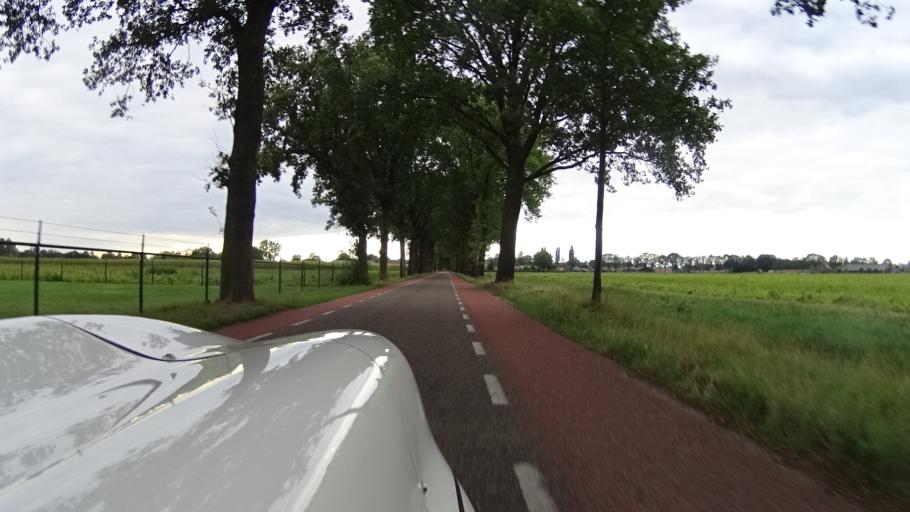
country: NL
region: North Brabant
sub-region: Gemeente Bernheze
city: Loosbroek
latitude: 51.6711
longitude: 5.5317
